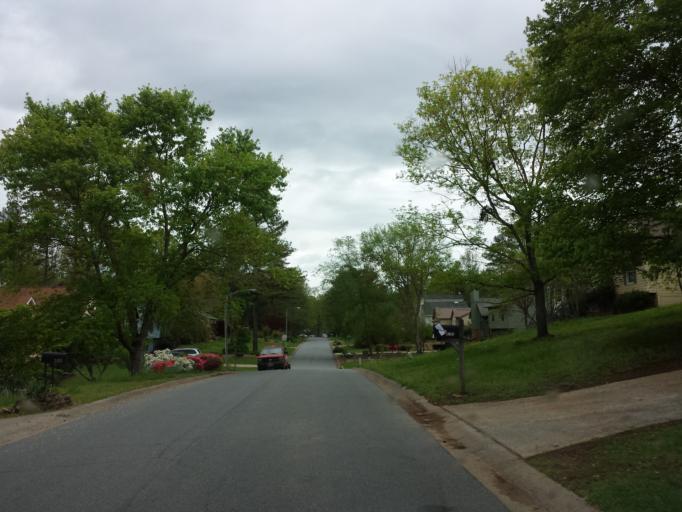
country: US
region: Georgia
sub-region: Cherokee County
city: Woodstock
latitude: 34.0375
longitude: -84.4861
